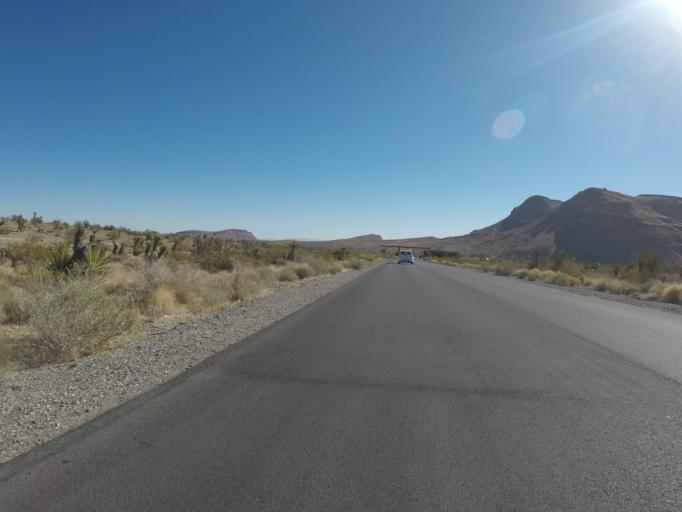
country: US
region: Nevada
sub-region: Clark County
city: Summerlin South
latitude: 36.1332
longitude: -115.4256
